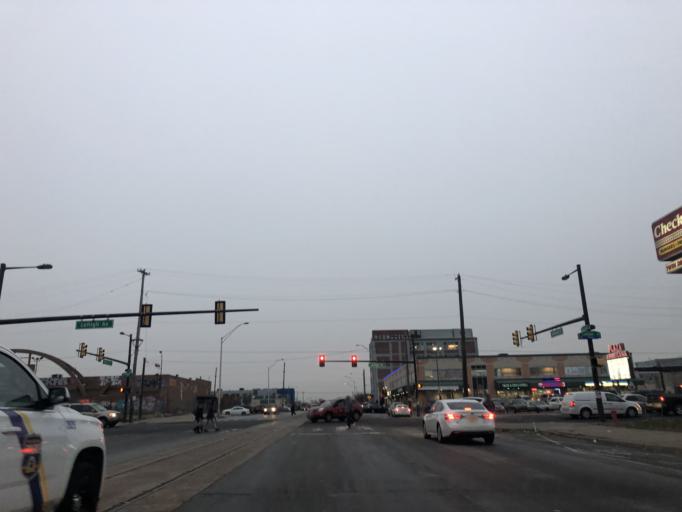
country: US
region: Pennsylvania
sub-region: Philadelphia County
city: Philadelphia
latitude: 39.9911
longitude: -75.1362
